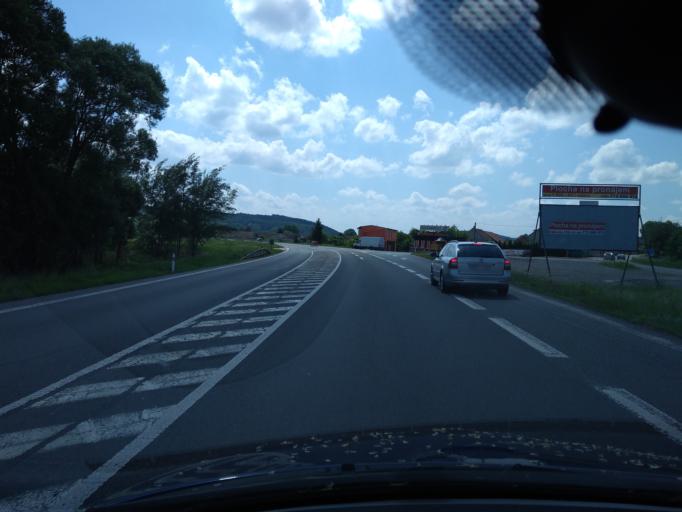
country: CZ
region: Plzensky
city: Svihov
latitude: 49.4860
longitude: 13.2863
